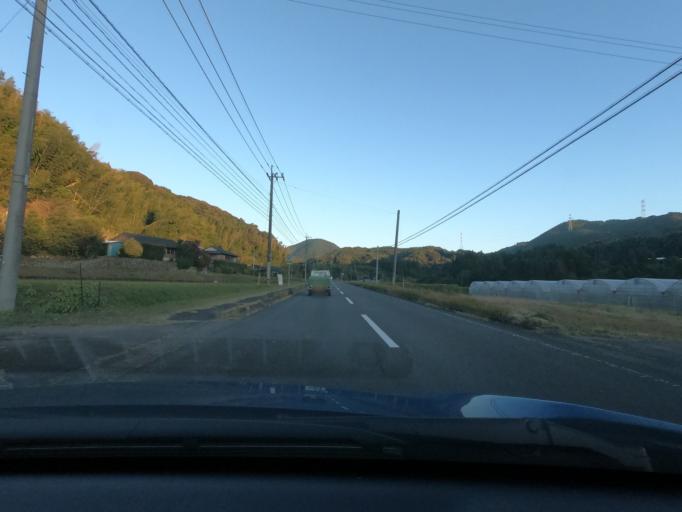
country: JP
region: Kagoshima
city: Satsumasendai
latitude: 31.7904
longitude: 130.4635
